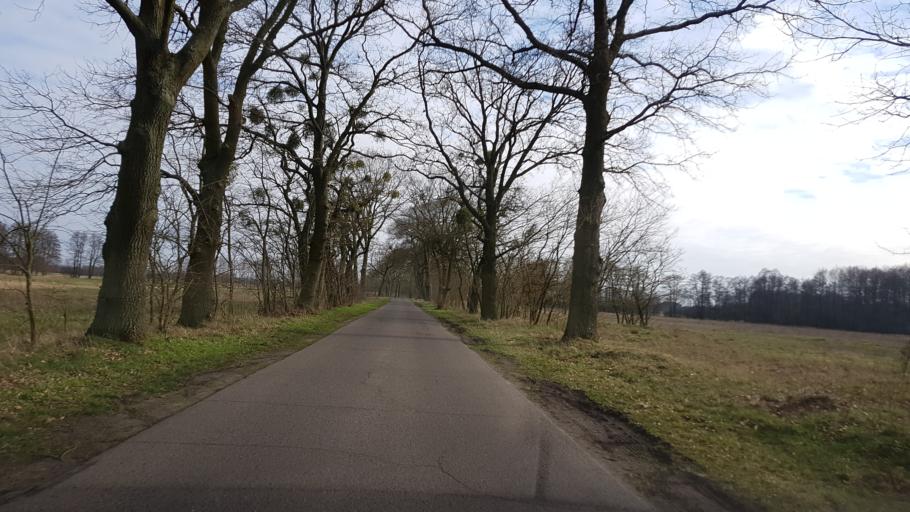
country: PL
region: West Pomeranian Voivodeship
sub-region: Powiat policki
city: Dobra
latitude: 53.5282
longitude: 14.3416
